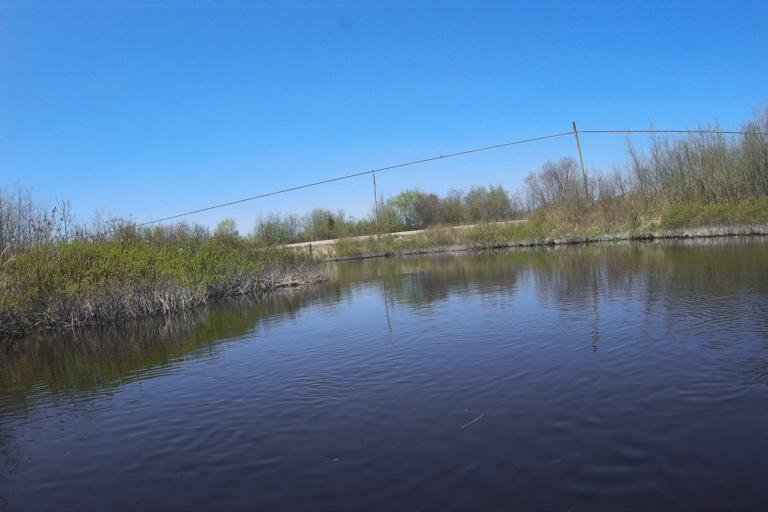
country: CA
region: Ontario
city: Powassan
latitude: 46.1558
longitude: -79.2459
